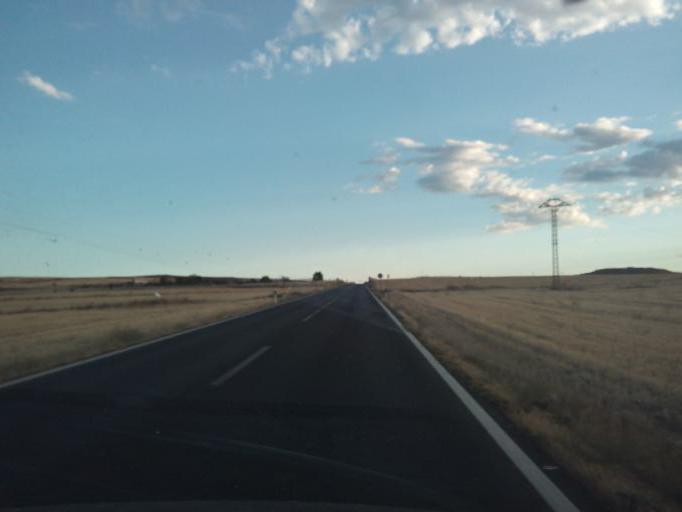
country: ES
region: Madrid
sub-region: Provincia de Madrid
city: Algete
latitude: 40.6127
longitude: -3.4844
